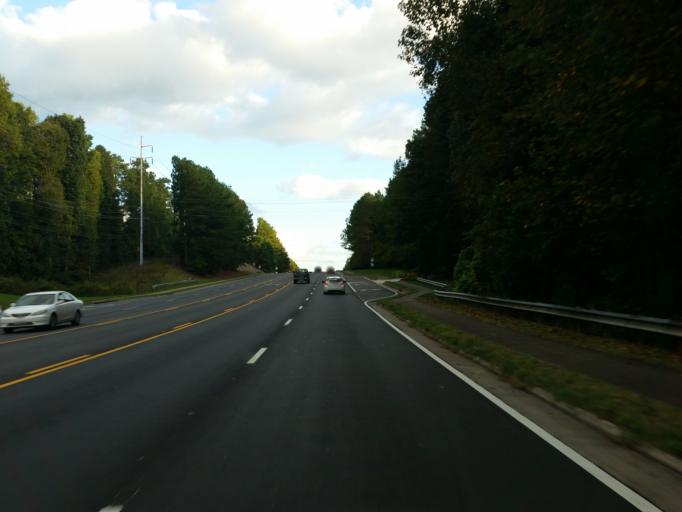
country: US
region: Georgia
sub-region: Cobb County
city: Smyrna
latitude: 33.8556
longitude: -84.5134
